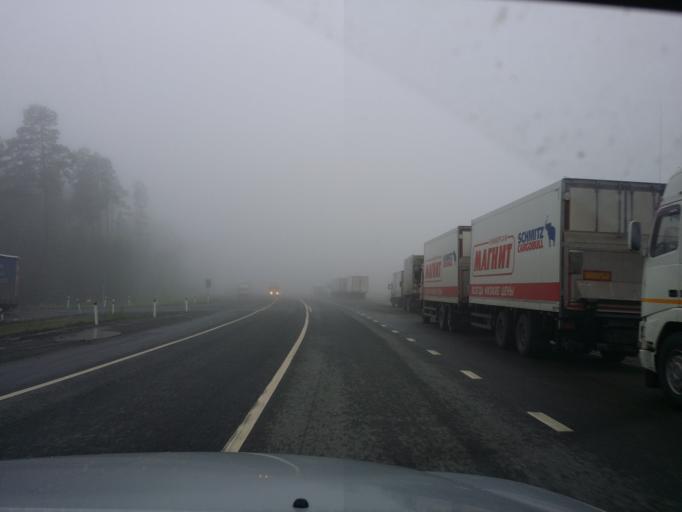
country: RU
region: Khanty-Mansiyskiy Avtonomnyy Okrug
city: Gornopravdinsk
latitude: 59.6926
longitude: 70.0949
